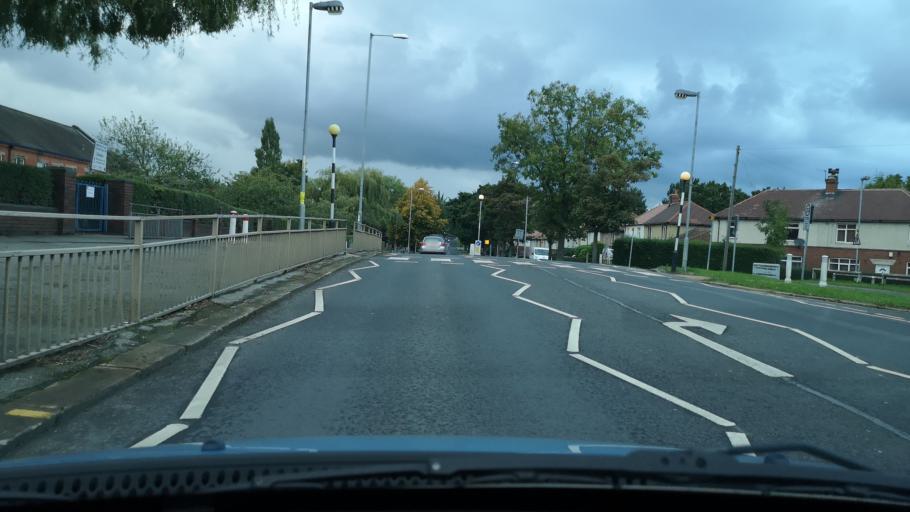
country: GB
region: England
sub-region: City and Borough of Wakefield
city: Horbury
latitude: 53.6717
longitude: -1.5366
